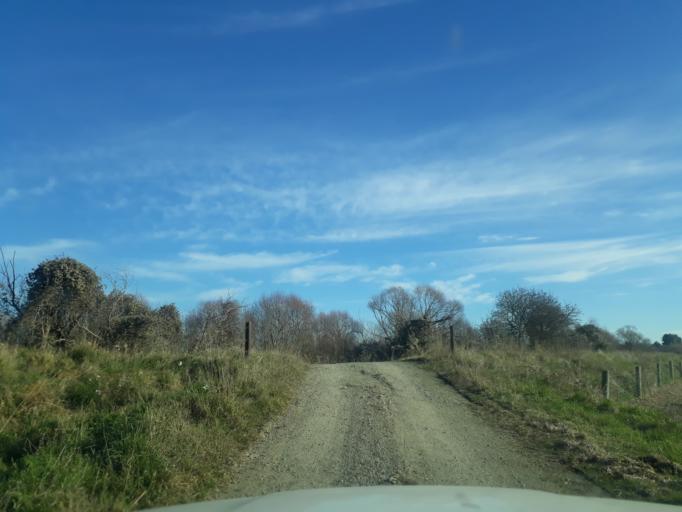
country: NZ
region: Canterbury
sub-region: Timaru District
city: Timaru
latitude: -44.2697
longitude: 171.3328
